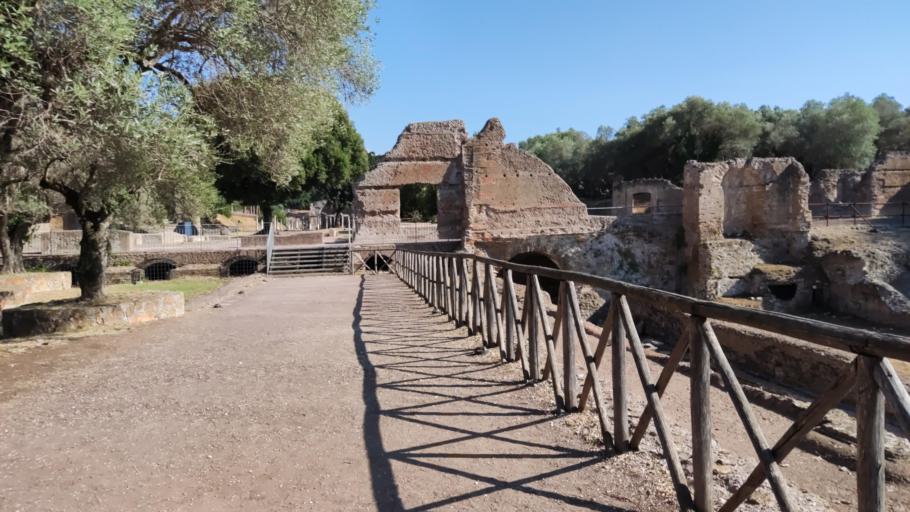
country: IT
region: Latium
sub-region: Citta metropolitana di Roma Capitale
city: Villa Adriana
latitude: 41.9404
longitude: 12.7747
